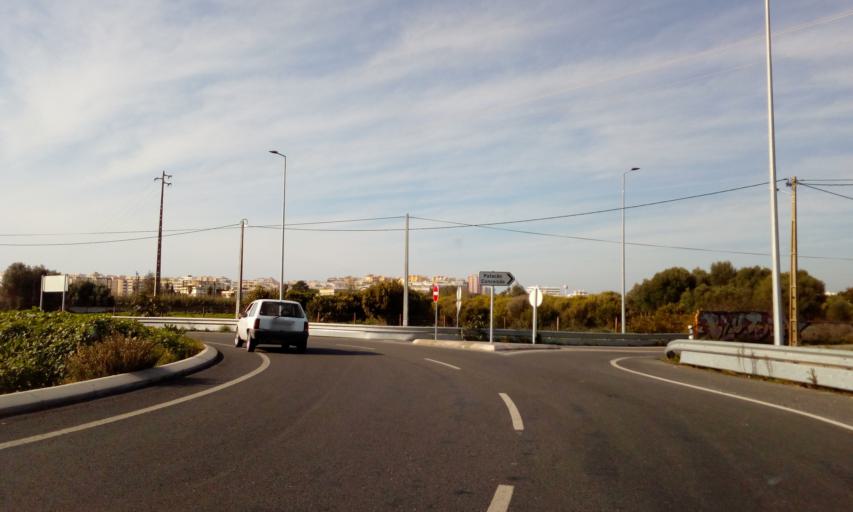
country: PT
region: Faro
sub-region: Faro
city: Faro
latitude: 37.0300
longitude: -7.9164
